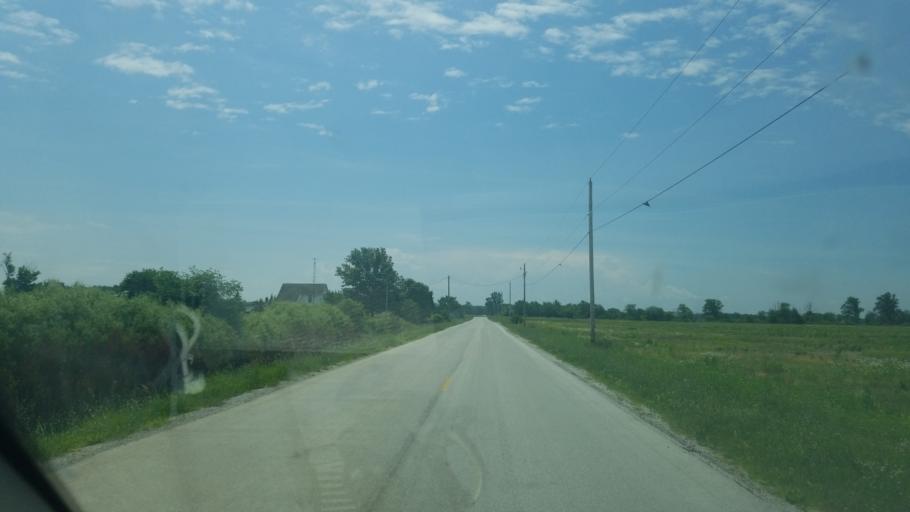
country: US
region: Ohio
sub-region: Wood County
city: North Baltimore
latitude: 41.1998
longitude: -83.5923
